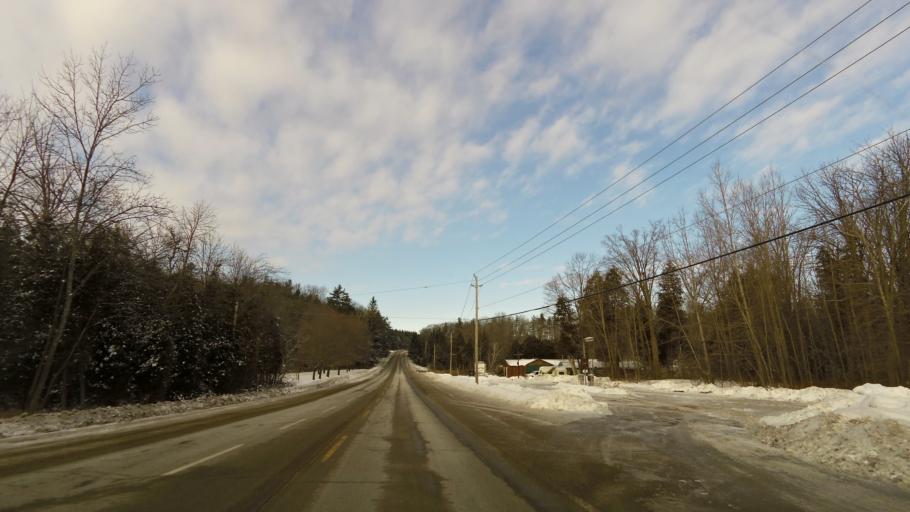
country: CA
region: Ontario
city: Quinte West
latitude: 44.1077
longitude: -77.7734
